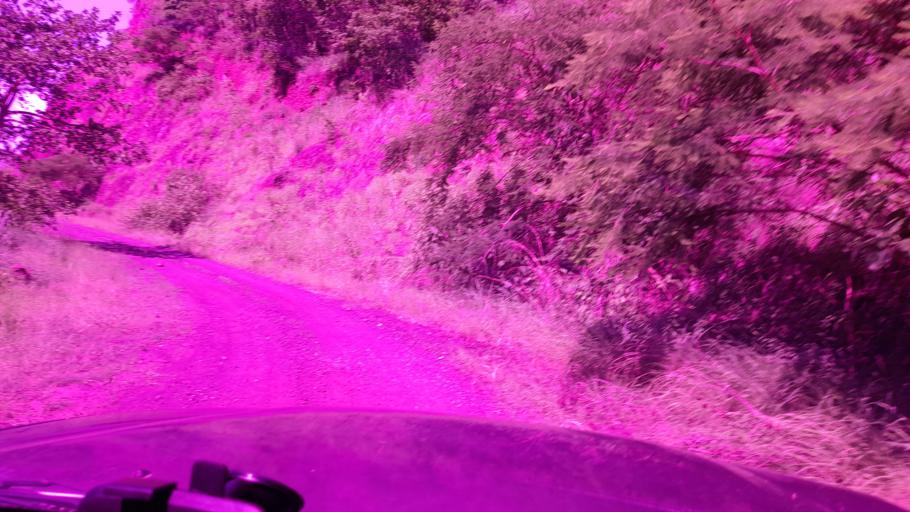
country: ET
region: Southern Nations, Nationalities, and People's Region
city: K'olito
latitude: 7.7724
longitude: 37.5537
